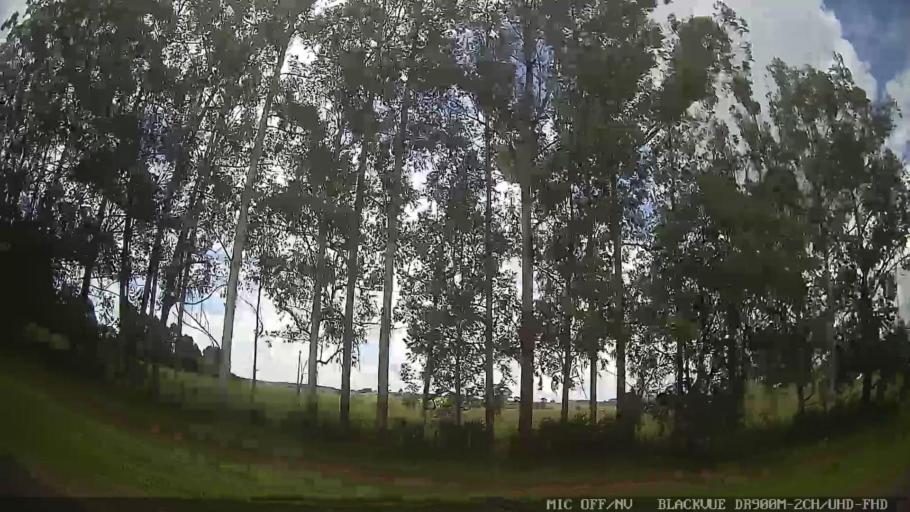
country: BR
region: Sao Paulo
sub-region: Laranjal Paulista
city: Laranjal Paulista
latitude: -23.0443
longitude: -47.9140
